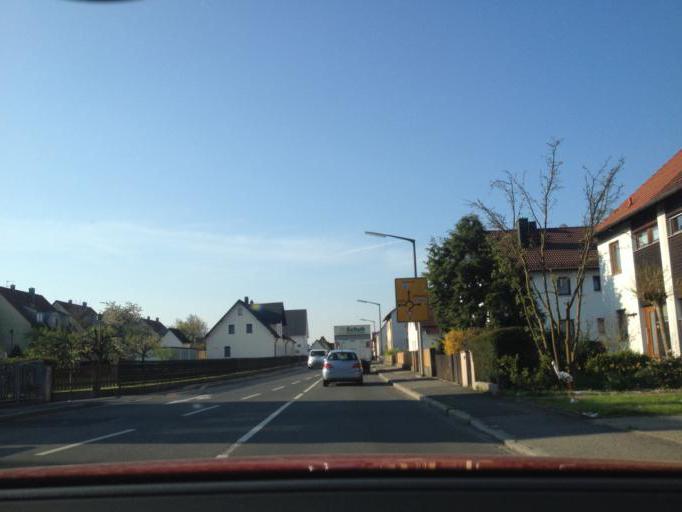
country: DE
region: Bavaria
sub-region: Regierungsbezirk Mittelfranken
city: Leinburg
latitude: 49.4629
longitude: 11.2871
